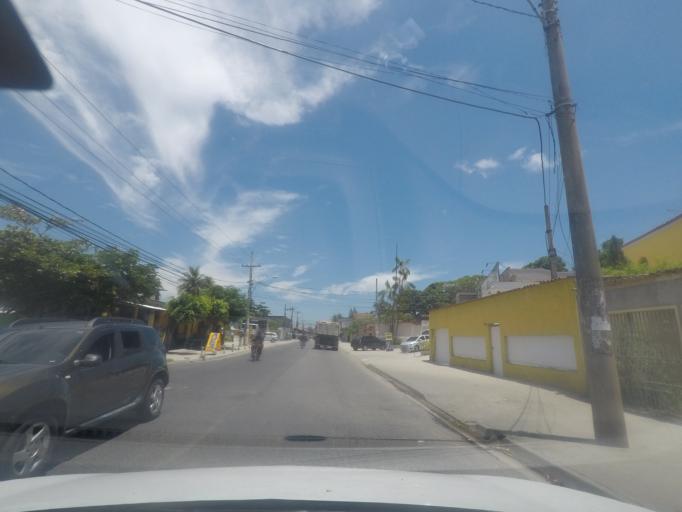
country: BR
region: Rio de Janeiro
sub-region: Itaguai
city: Itaguai
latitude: -22.9286
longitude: -43.6902
